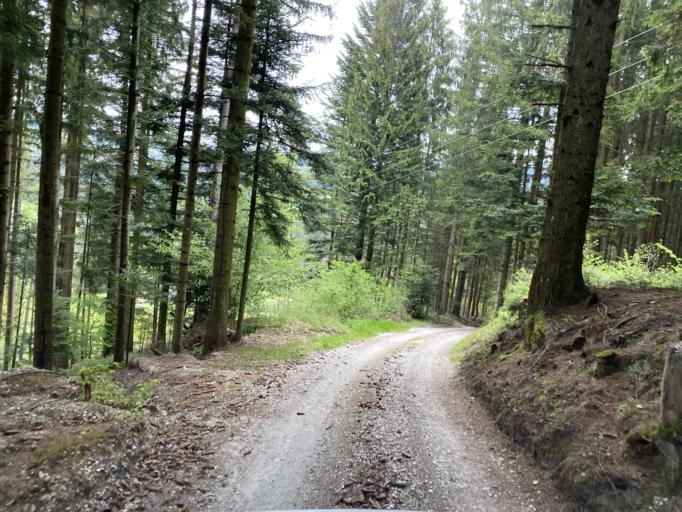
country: AT
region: Styria
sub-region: Politischer Bezirk Weiz
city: Gschaid bei Birkfeld
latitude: 47.3652
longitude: 15.7283
